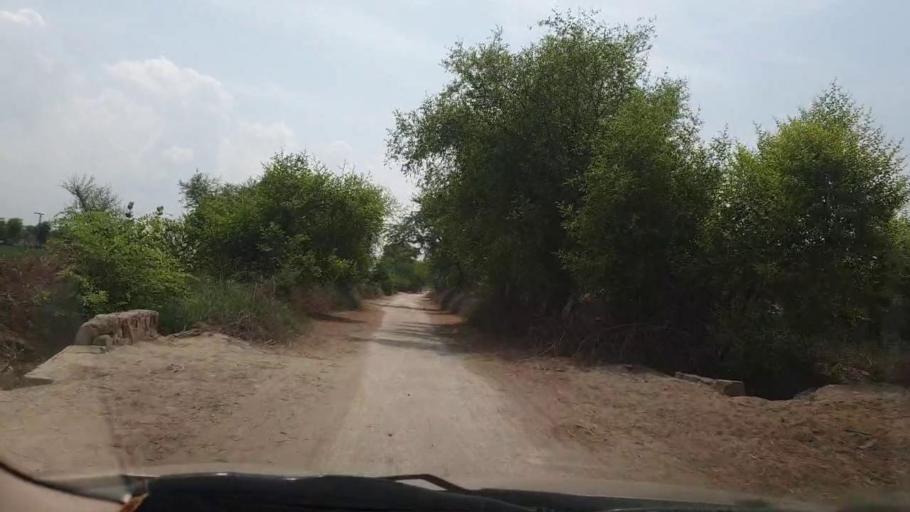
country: PK
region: Sindh
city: Larkana
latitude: 27.5842
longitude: 68.1166
